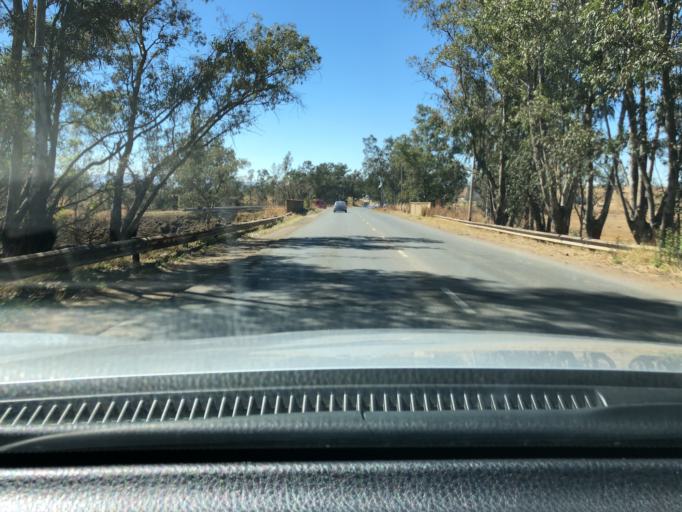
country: ZA
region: KwaZulu-Natal
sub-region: Amajuba District Municipality
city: Newcastle
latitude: -27.7623
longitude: 29.9555
